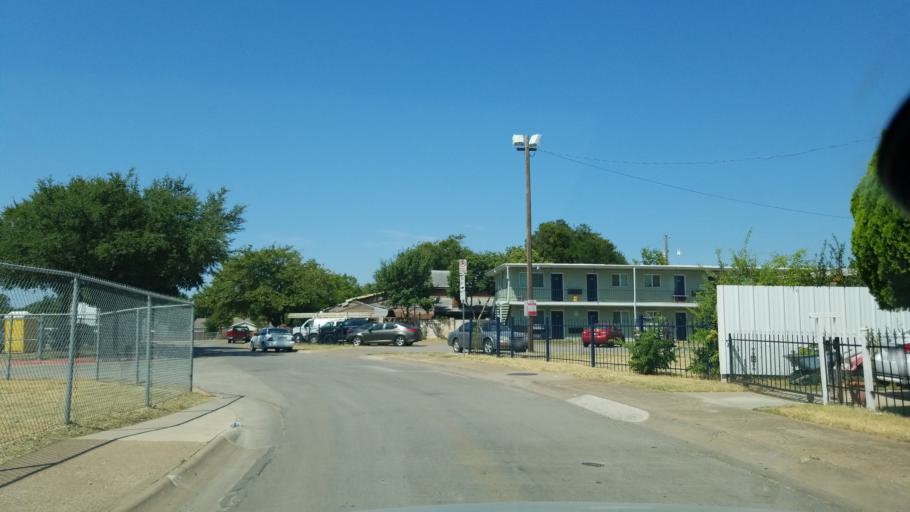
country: US
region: Texas
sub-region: Dallas County
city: Cockrell Hill
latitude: 32.7435
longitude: -96.8850
